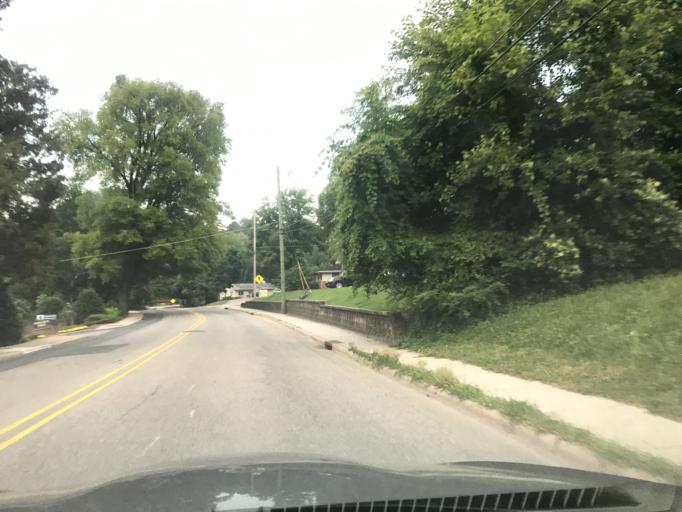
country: US
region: North Carolina
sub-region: Orange County
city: Chapel Hill
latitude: 35.9244
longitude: -79.0525
